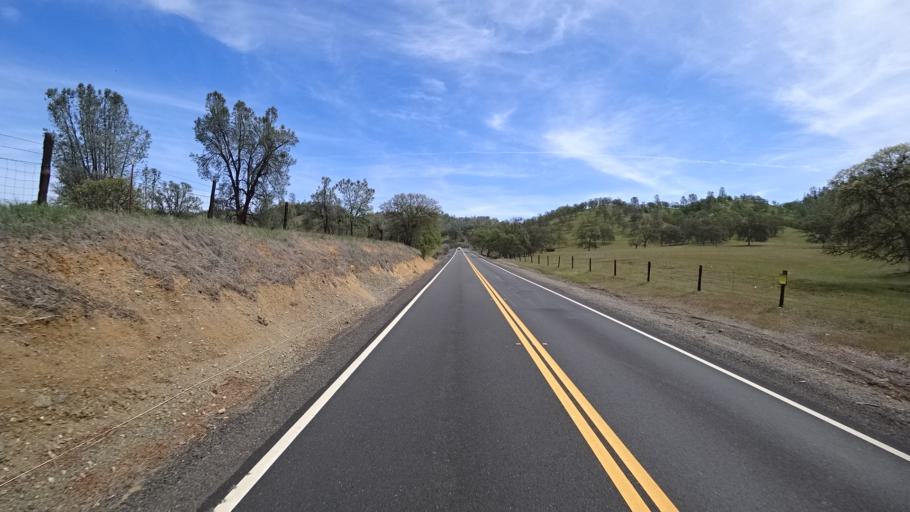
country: US
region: California
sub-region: Glenn County
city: Willows
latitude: 39.6146
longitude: -122.5175
